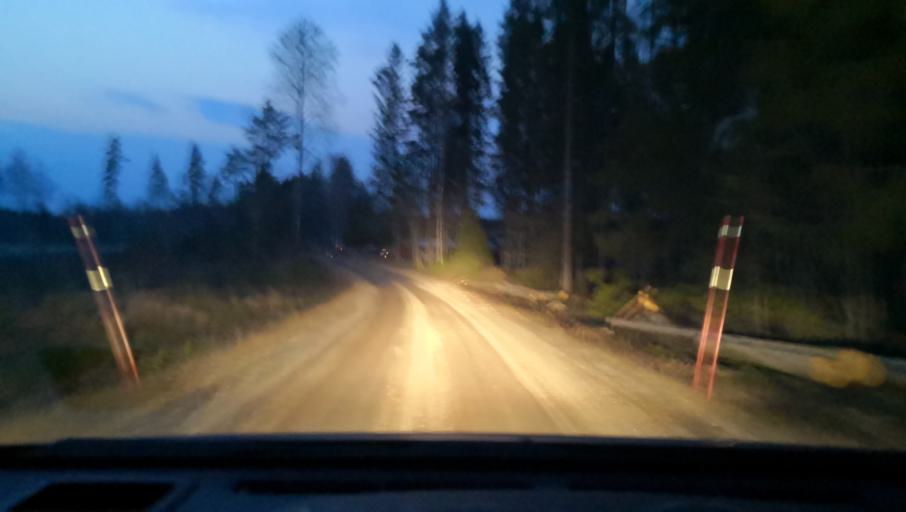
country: SE
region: OErebro
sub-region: Lindesbergs Kommun
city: Frovi
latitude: 59.5925
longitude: 15.4699
